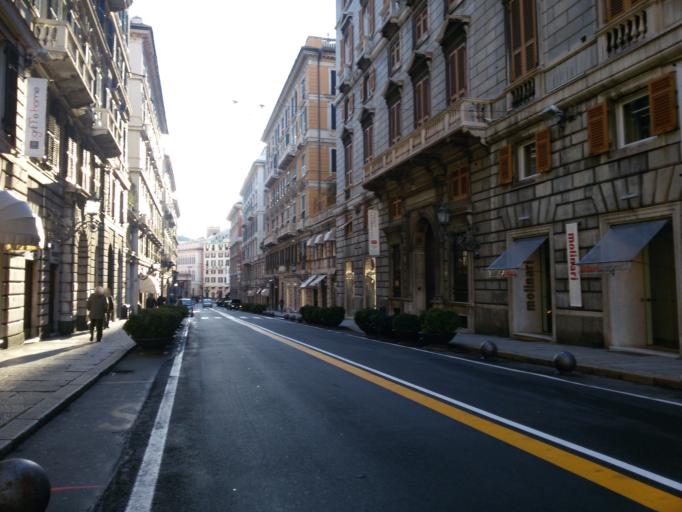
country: IT
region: Liguria
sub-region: Provincia di Genova
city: San Teodoro
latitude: 44.4094
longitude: 8.9367
